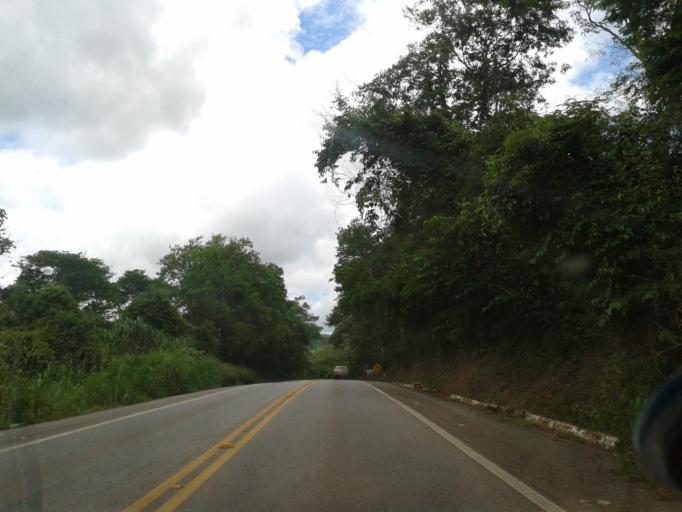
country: BR
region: Goias
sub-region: Goias
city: Goias
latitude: -15.9369
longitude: -50.1345
